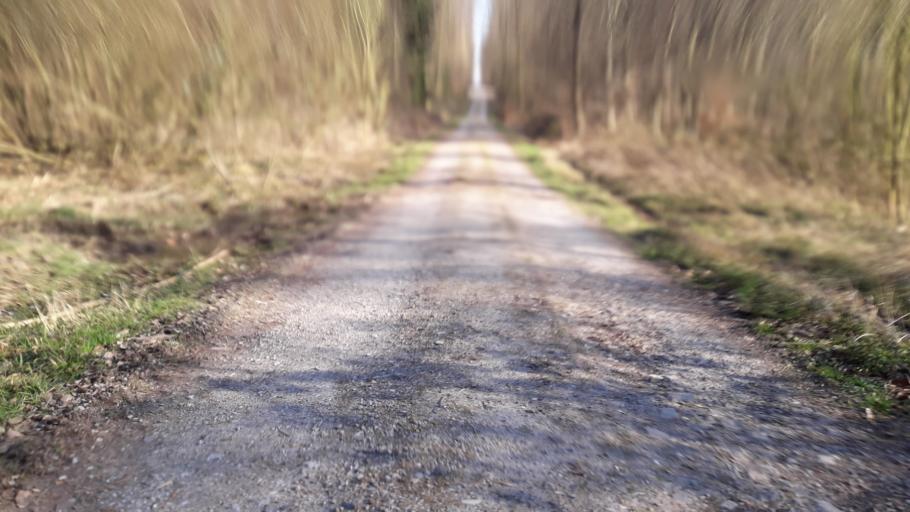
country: DE
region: North Rhine-Westphalia
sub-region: Regierungsbezirk Detmold
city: Salzkotten
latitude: 51.6657
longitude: 8.6640
